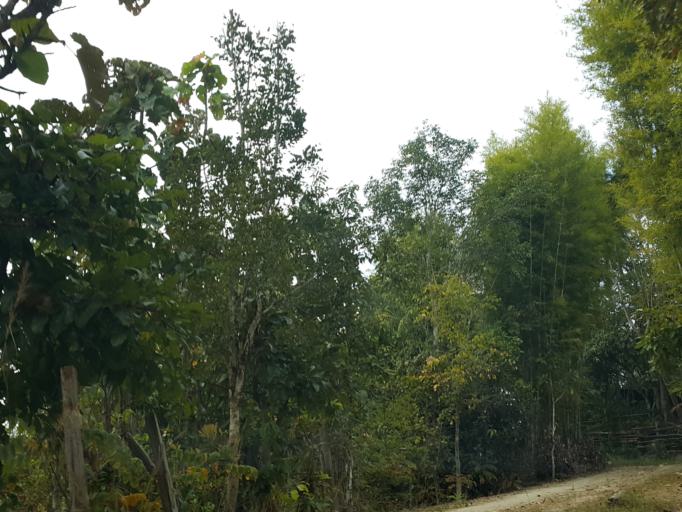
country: TH
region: Chiang Mai
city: Om Koi
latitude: 17.7979
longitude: 98.3365
